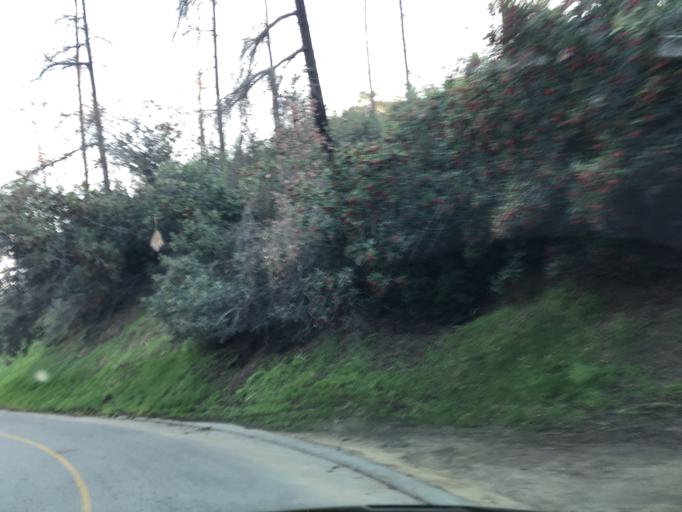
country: US
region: California
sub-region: Los Angeles County
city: Echo Park
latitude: 34.0804
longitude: -118.2325
